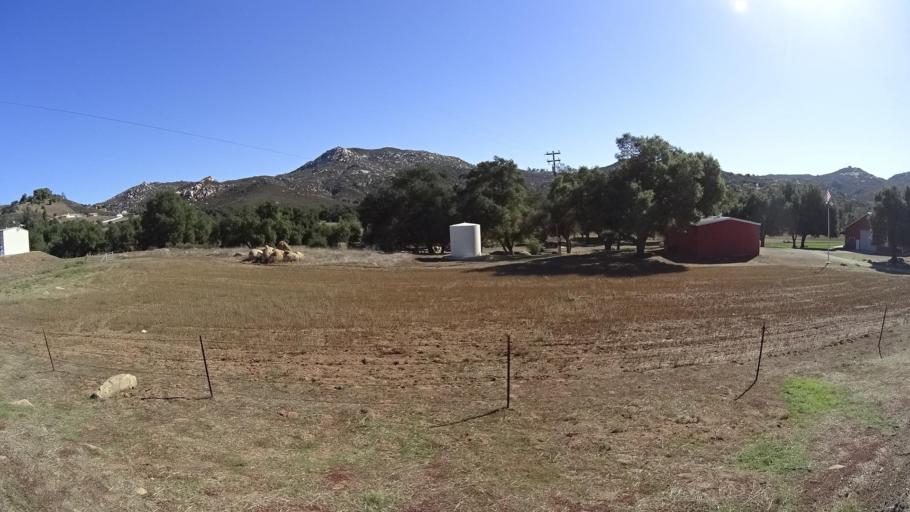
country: US
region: California
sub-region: San Diego County
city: Jamul
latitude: 32.6818
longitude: -116.7538
